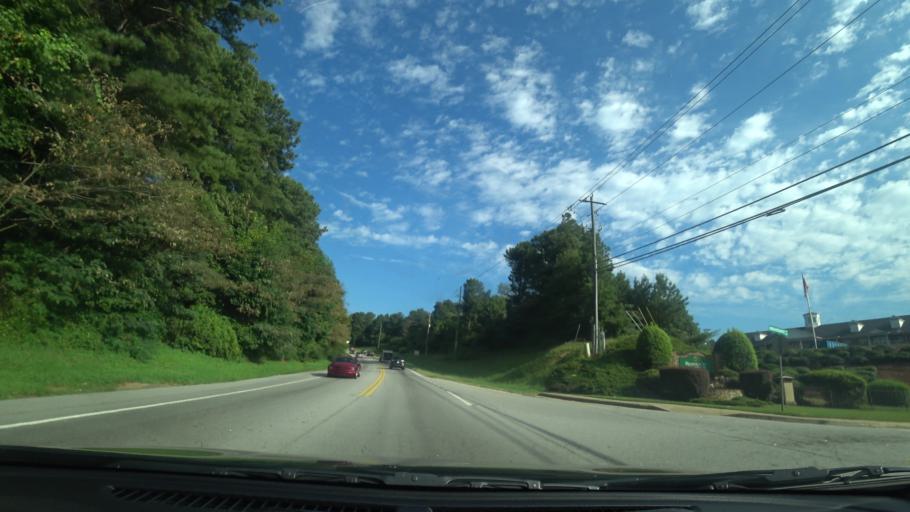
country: US
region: Georgia
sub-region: Rockdale County
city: Conyers
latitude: 33.6795
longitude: -83.9910
